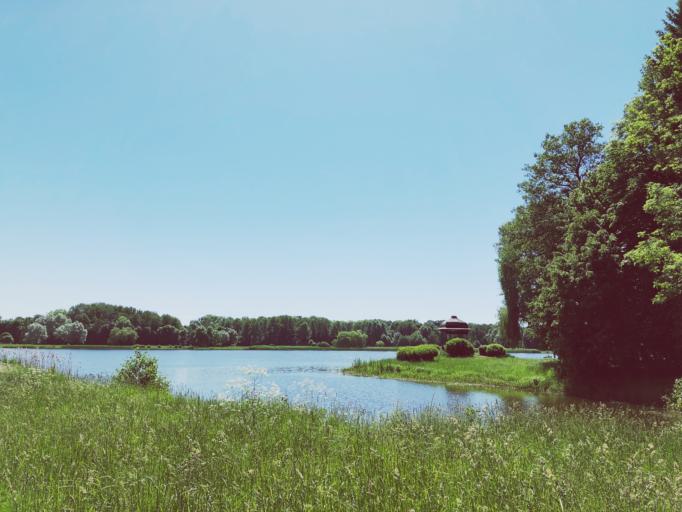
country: BY
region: Minsk
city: Nyasvizh
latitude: 53.2286
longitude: 26.6975
